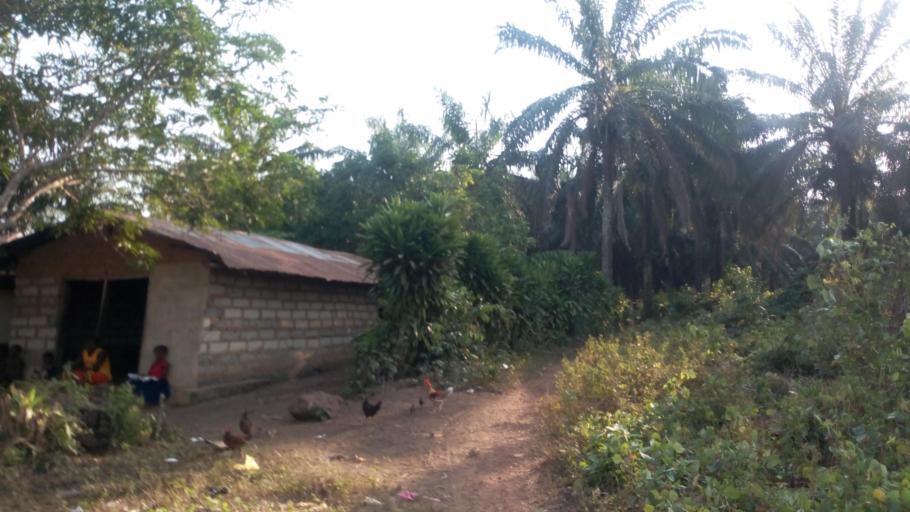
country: SL
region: Southern Province
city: Mogbwemo
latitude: 7.5996
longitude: -12.1720
